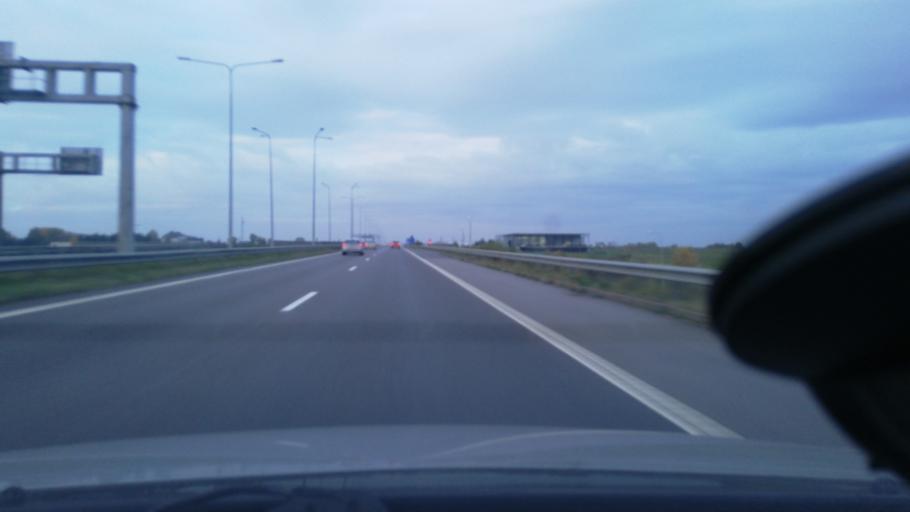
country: LT
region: Klaipedos apskritis
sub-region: Klaipeda
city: Klaipeda
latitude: 55.7061
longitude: 21.2319
